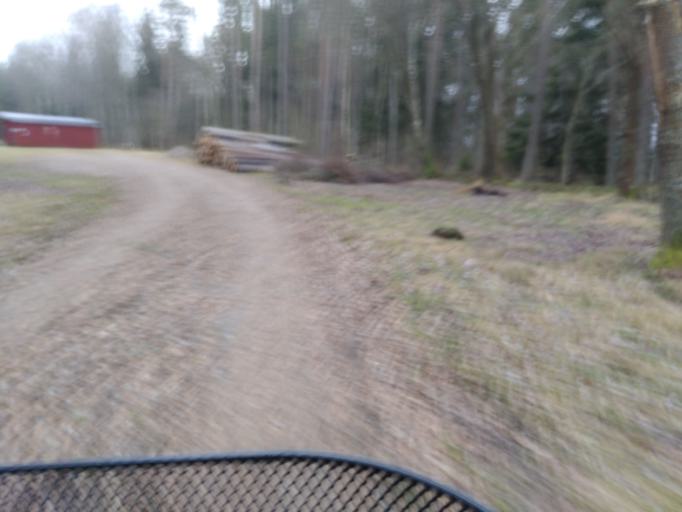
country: SE
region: Vaestra Goetaland
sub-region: Lidkopings Kommun
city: Lidkoping
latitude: 58.4856
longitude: 13.1491
